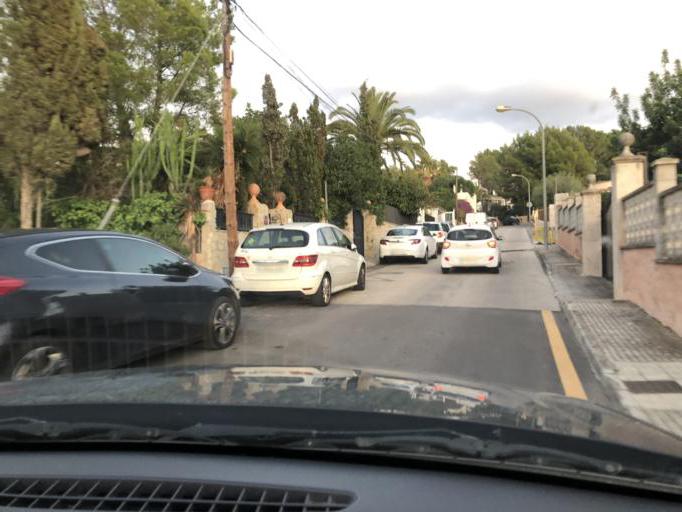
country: ES
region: Balearic Islands
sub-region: Illes Balears
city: Santa Ponsa
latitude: 39.5267
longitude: 2.4825
